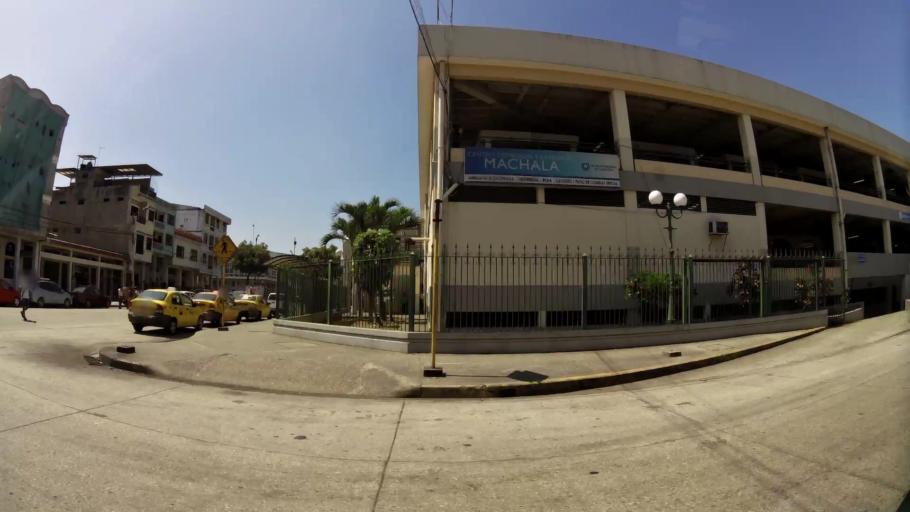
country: EC
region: Guayas
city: Guayaquil
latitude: -2.1965
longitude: -79.8930
